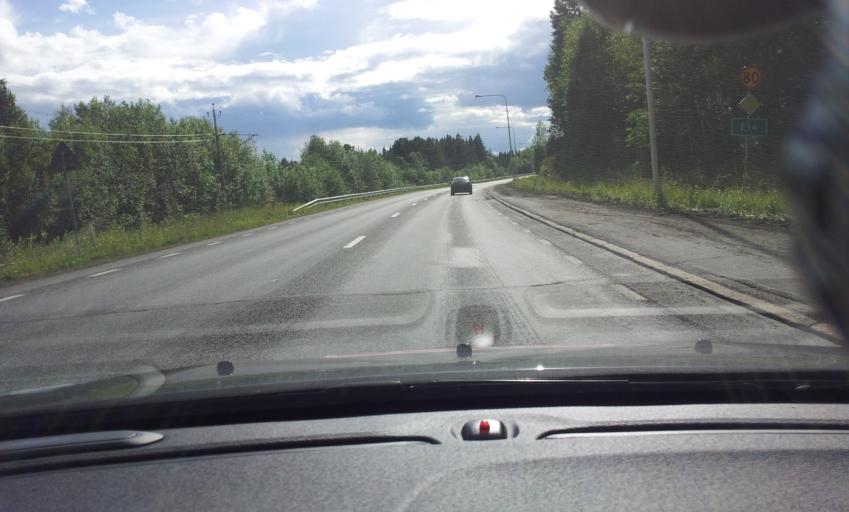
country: SE
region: Jaemtland
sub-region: Are Kommun
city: Jarpen
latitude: 63.3404
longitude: 13.4439
